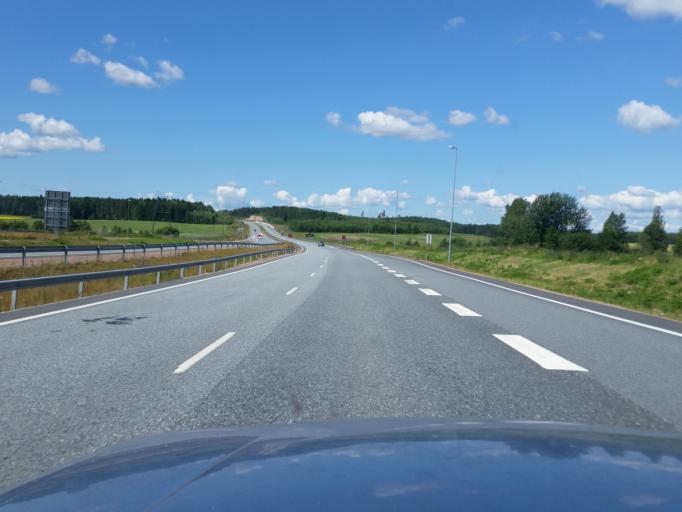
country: FI
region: Varsinais-Suomi
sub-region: Salo
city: Kiikala
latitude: 60.3899
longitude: 23.5821
